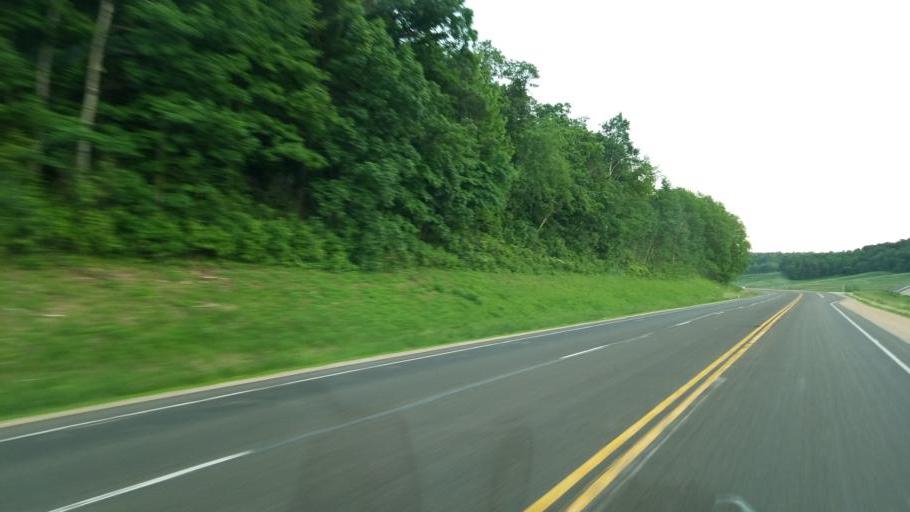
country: US
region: Wisconsin
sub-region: Monroe County
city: Tomah
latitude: 43.8816
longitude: -90.4810
